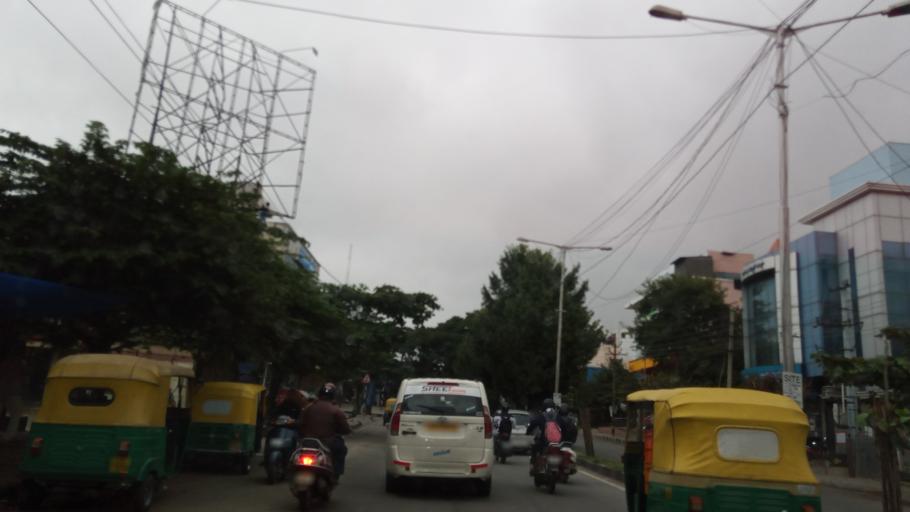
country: IN
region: Karnataka
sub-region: Bangalore Urban
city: Bangalore
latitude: 12.9236
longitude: 77.5543
